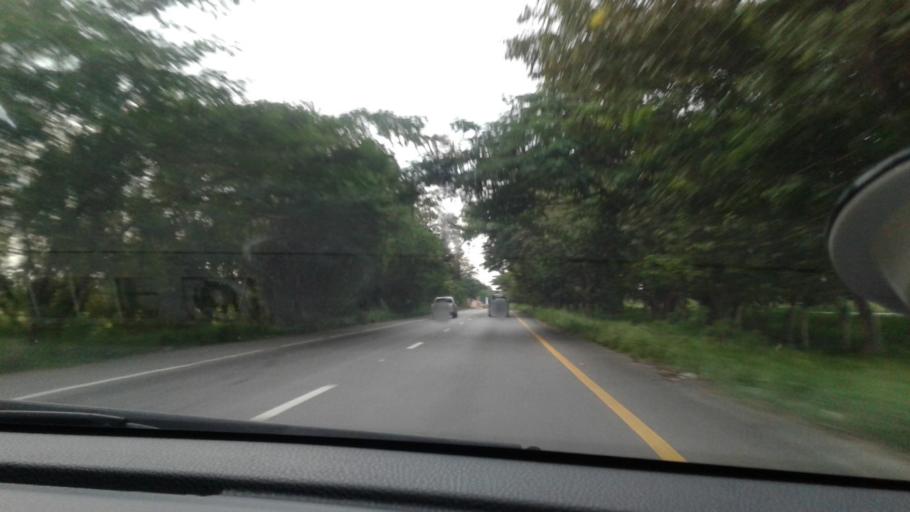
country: TH
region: Prachuap Khiri Khan
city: Hua Hin
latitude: 12.5495
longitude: 99.8733
